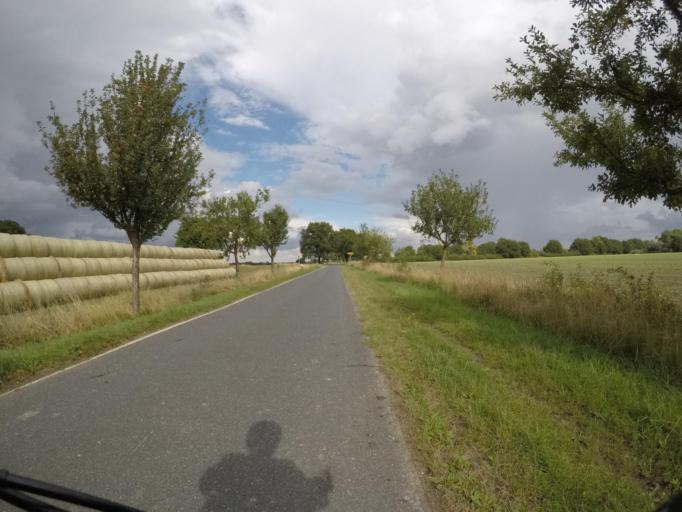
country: DE
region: Lower Saxony
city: Neu Darchau
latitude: 53.2630
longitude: 10.8435
